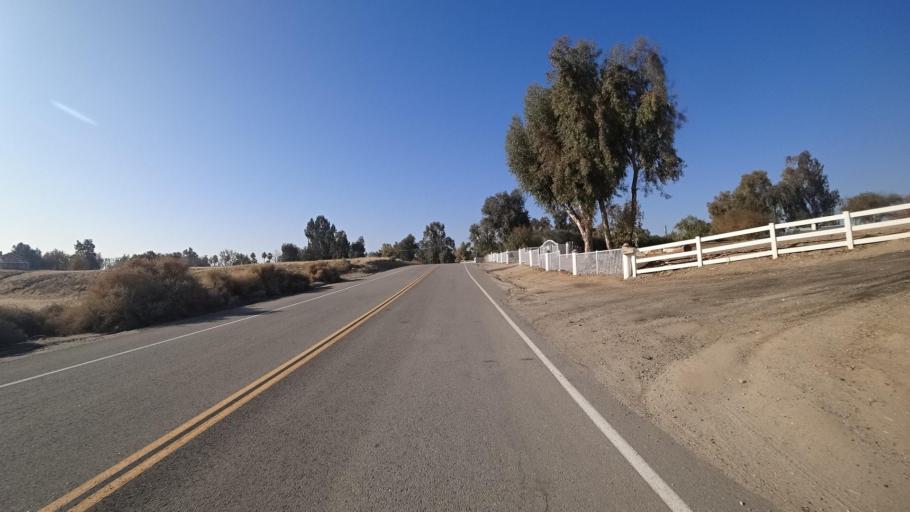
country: US
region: California
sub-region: Kern County
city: Oildale
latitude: 35.4531
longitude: -118.9072
